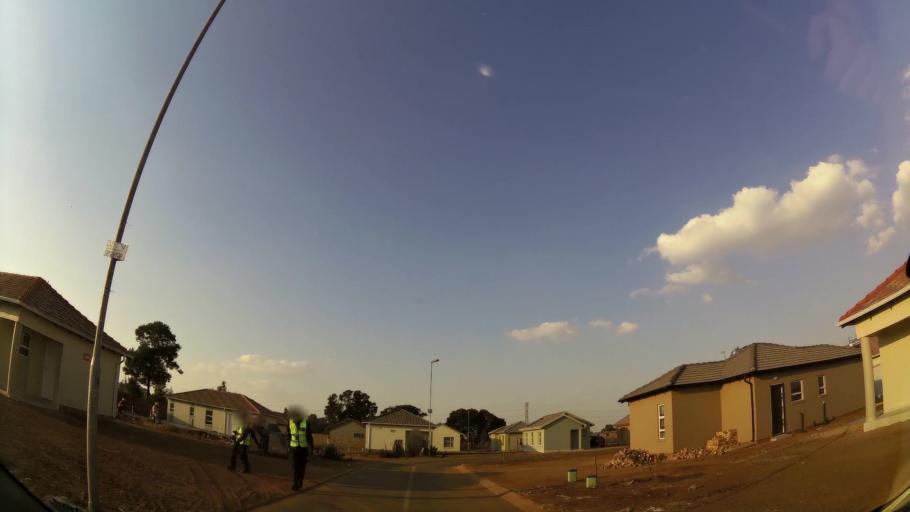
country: ZA
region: Gauteng
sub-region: Ekurhuleni Metropolitan Municipality
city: Benoni
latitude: -26.1261
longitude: 28.3797
